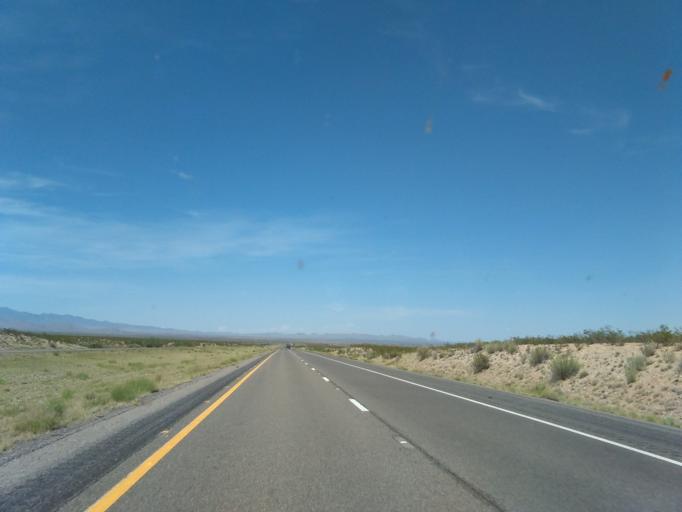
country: US
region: New Mexico
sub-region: Sierra County
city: Elephant Butte
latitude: 33.5785
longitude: -107.1673
